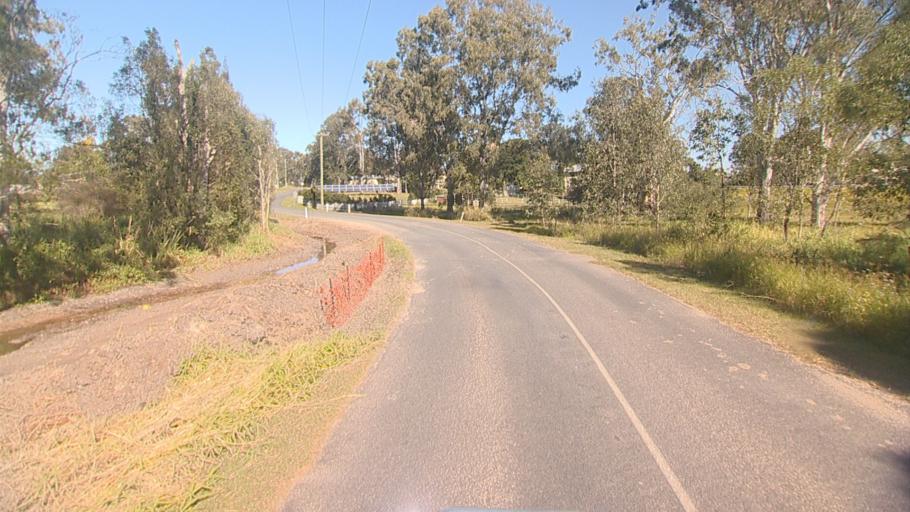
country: AU
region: Queensland
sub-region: Logan
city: Waterford West
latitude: -27.6976
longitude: 153.1480
